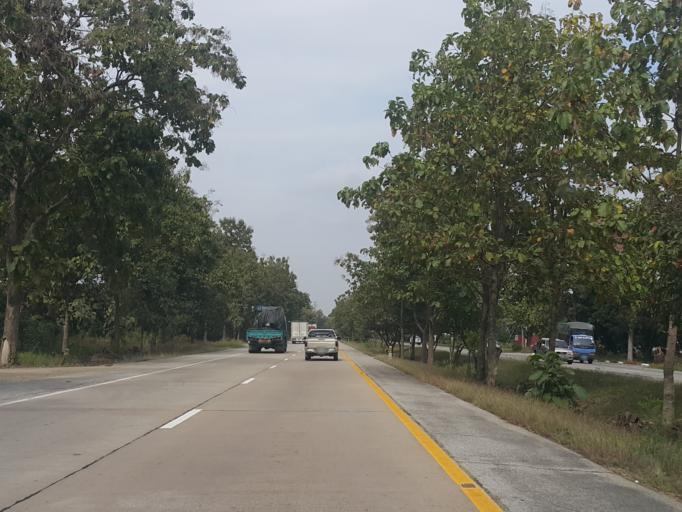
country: TH
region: Lamphun
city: Lamphun
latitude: 18.5325
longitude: 99.0772
